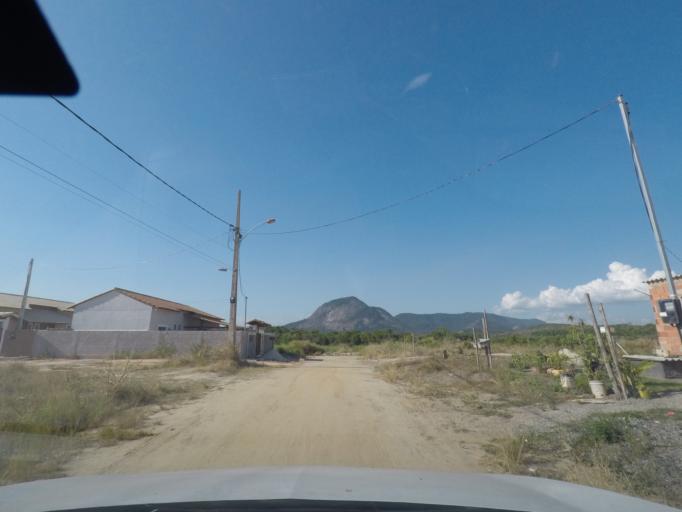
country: BR
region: Rio de Janeiro
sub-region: Marica
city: Marica
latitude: -22.9656
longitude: -42.9127
